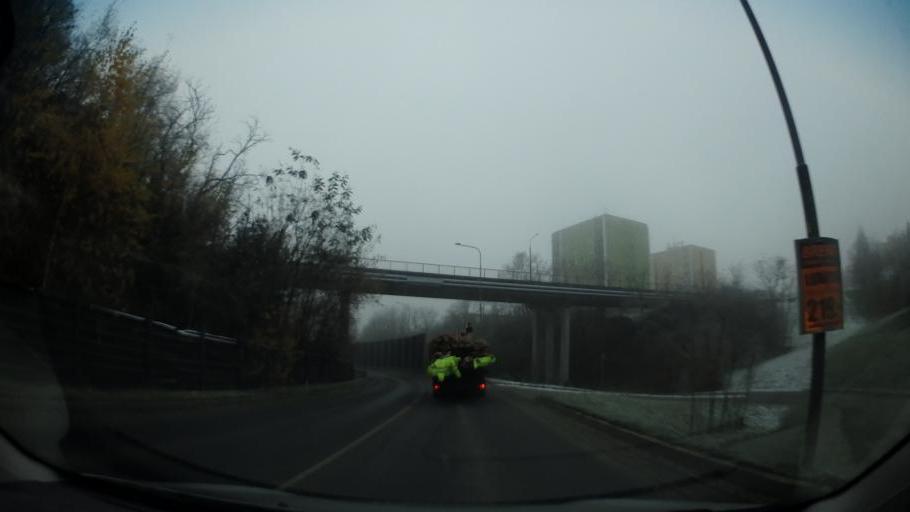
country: CZ
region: Vysocina
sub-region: Okres Trebic
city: Trebic
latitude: 49.2190
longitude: 15.9003
